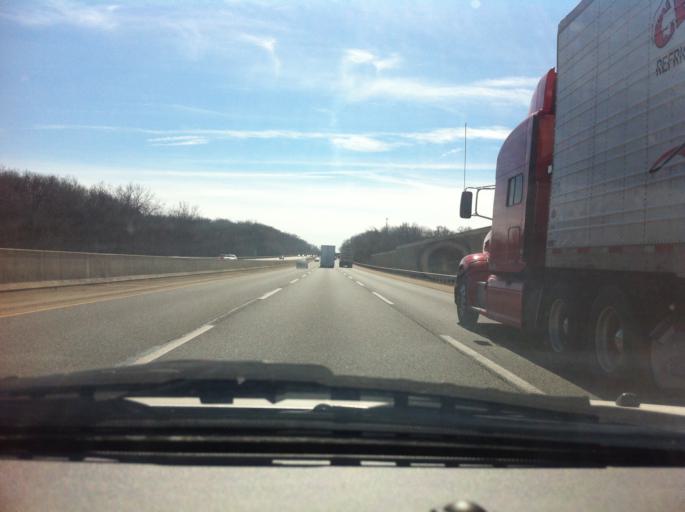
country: US
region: Illinois
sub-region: Winnebago County
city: Roscoe
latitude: 42.4511
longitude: -88.9948
